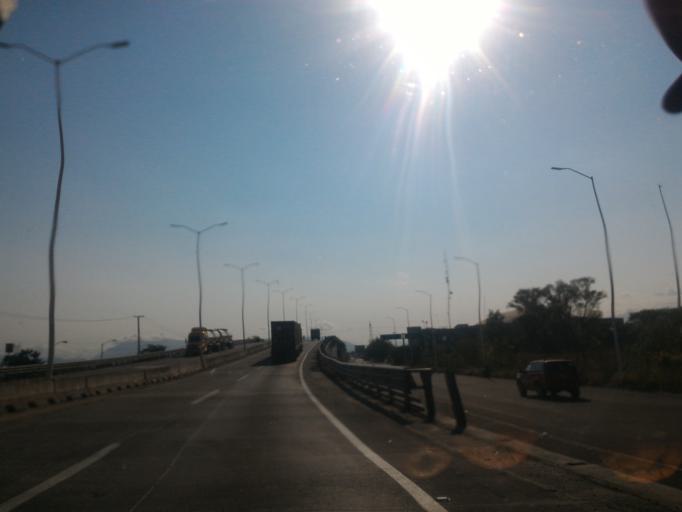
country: MX
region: Colima
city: Colima
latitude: 19.2565
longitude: -103.6854
